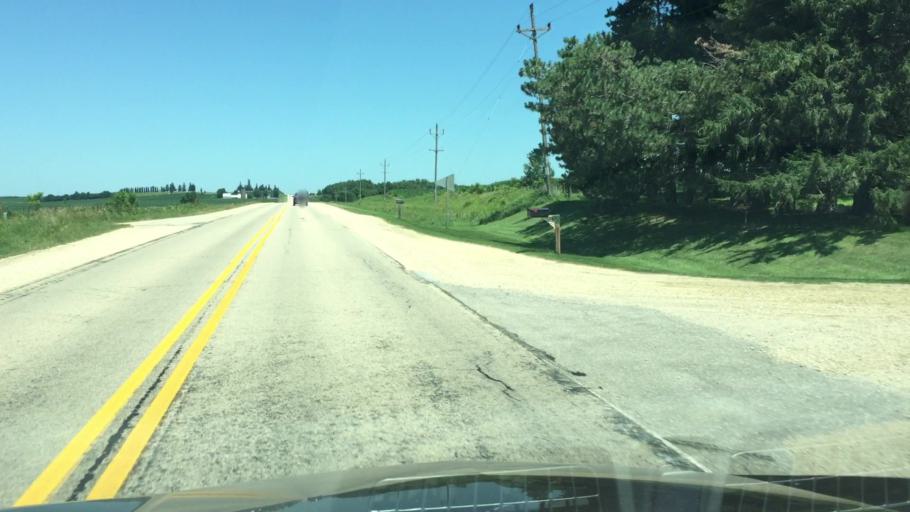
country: US
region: Iowa
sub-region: Cedar County
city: Mechanicsville
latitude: 41.9658
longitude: -91.1421
